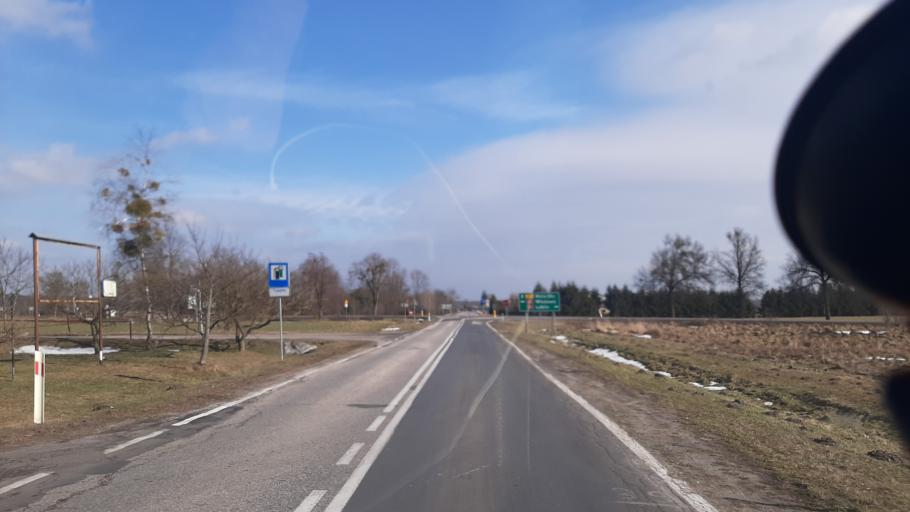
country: PL
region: Lublin Voivodeship
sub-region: Powiat wlodawski
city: Hansk
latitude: 51.4709
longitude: 23.3216
